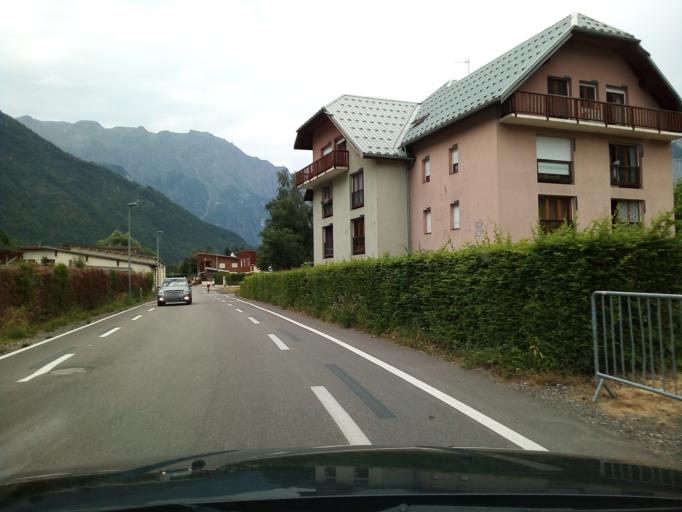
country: FR
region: Rhone-Alpes
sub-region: Departement de l'Isere
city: Huez
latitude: 45.0549
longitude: 6.0353
